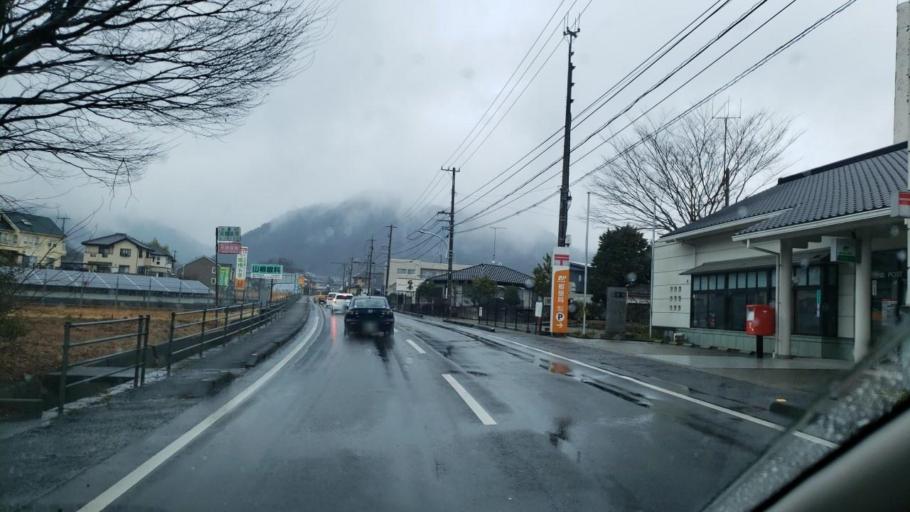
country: JP
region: Tokushima
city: Narutocho-mitsuishi
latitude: 34.1590
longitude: 134.5370
